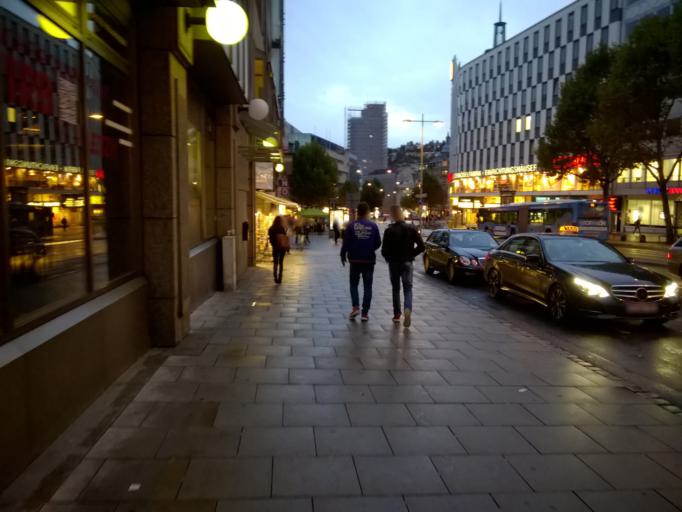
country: DE
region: Baden-Wuerttemberg
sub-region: Regierungsbezirk Stuttgart
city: Stuttgart
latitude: 48.7744
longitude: 9.1727
